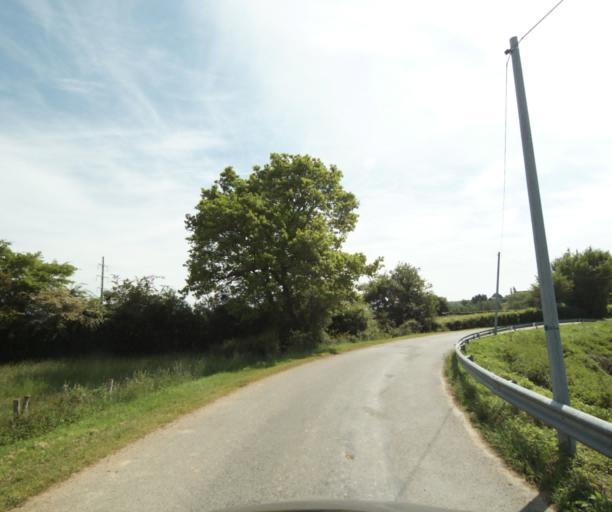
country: FR
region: Bourgogne
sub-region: Departement de Saone-et-Loire
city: Palinges
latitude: 46.5431
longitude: 4.1387
